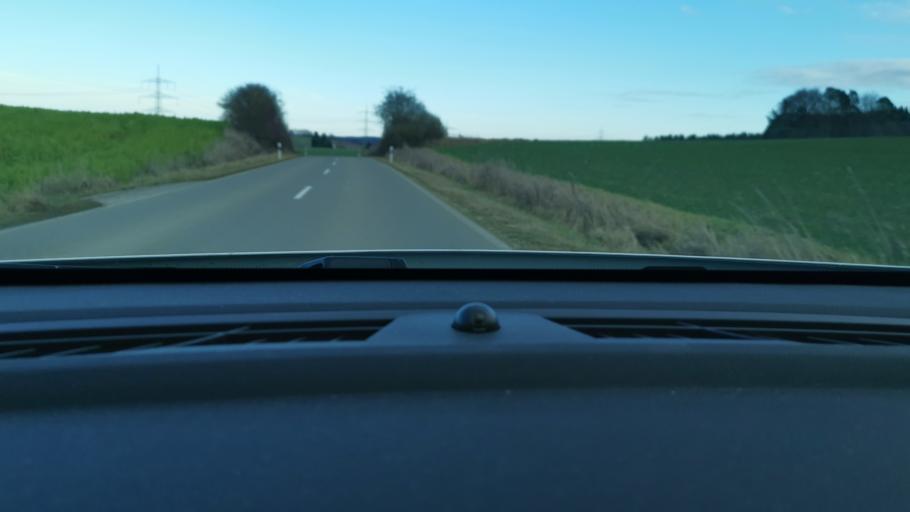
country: DE
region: Bavaria
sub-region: Swabia
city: Rehling
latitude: 48.4893
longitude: 10.9572
